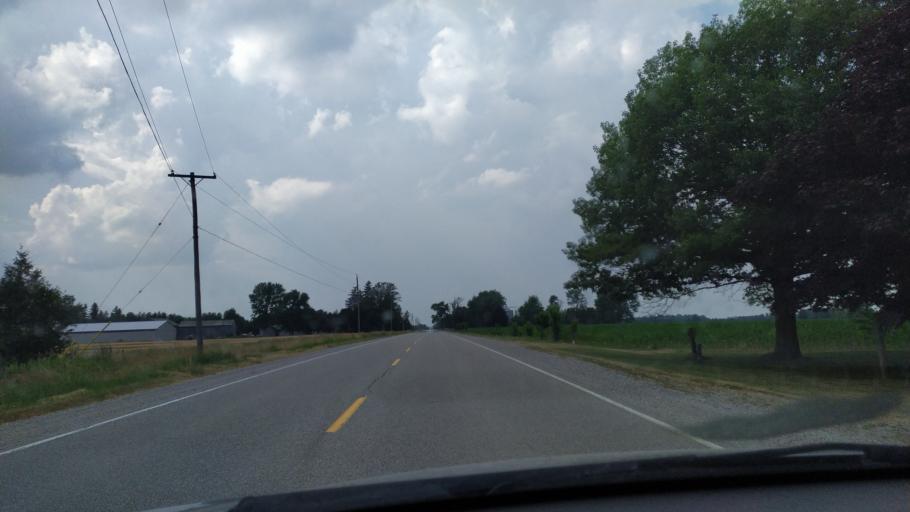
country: CA
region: Ontario
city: Dorchester
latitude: 43.1775
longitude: -81.1408
